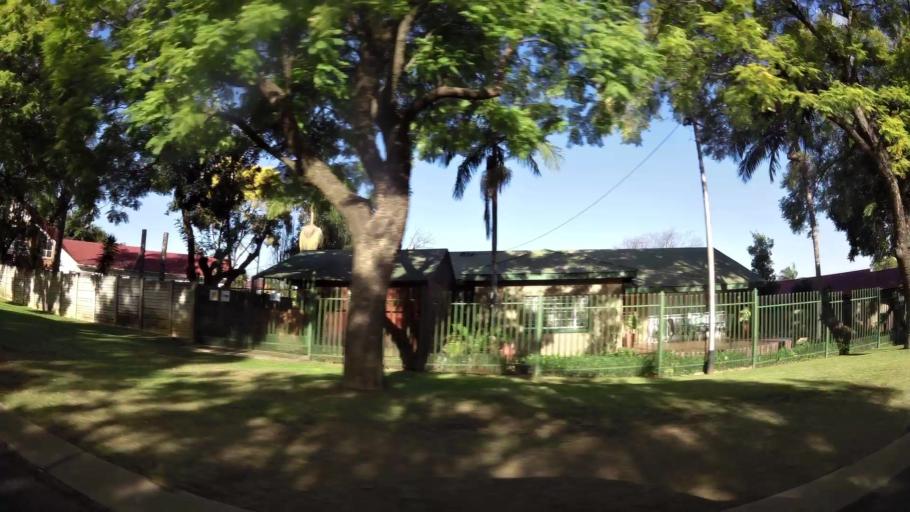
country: ZA
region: Gauteng
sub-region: City of Tshwane Metropolitan Municipality
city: Pretoria
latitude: -25.6998
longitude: 28.2349
